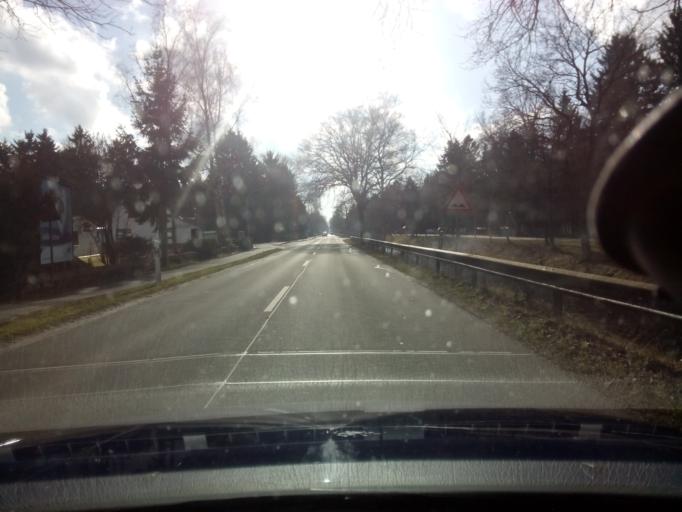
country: DE
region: Lower Saxony
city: Gnarrenburg
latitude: 53.3992
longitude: 9.0336
